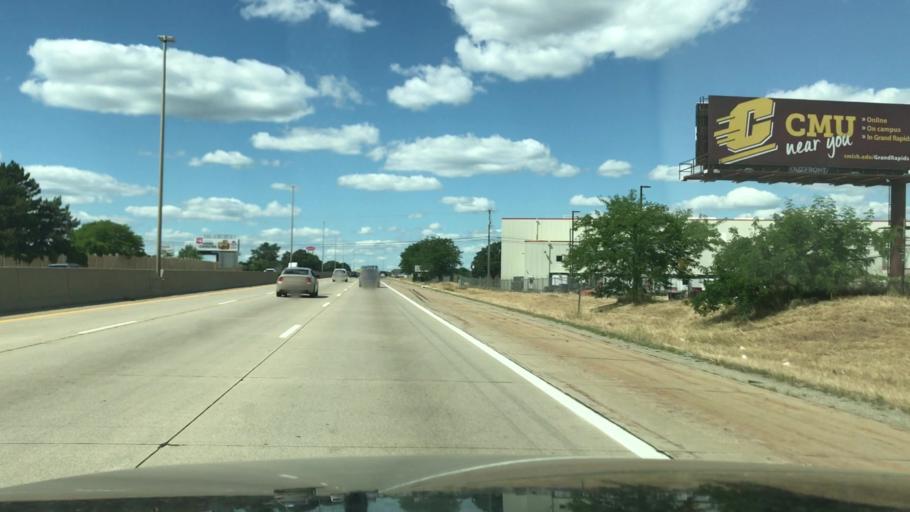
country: US
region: Michigan
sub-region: Kent County
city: Cutlerville
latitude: 42.8718
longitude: -85.6808
